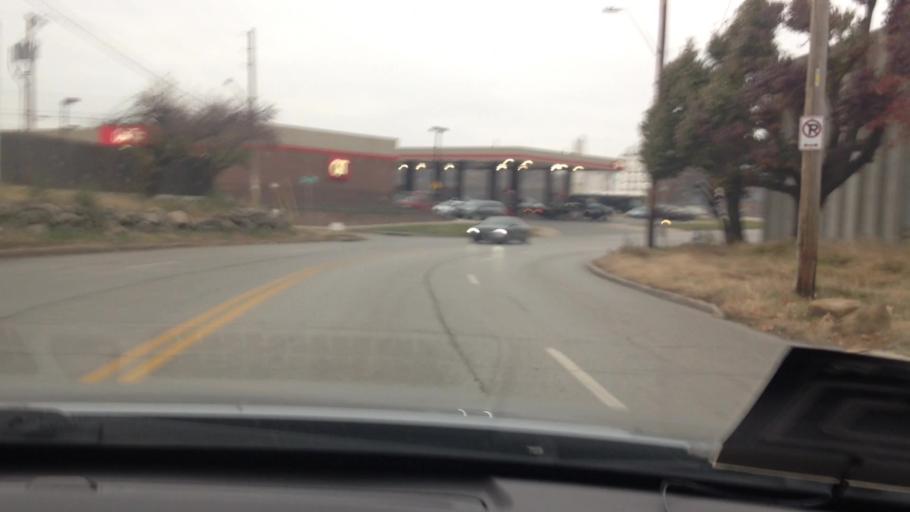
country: US
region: Kansas
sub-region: Johnson County
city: Westwood
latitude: 39.0718
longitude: -94.6061
